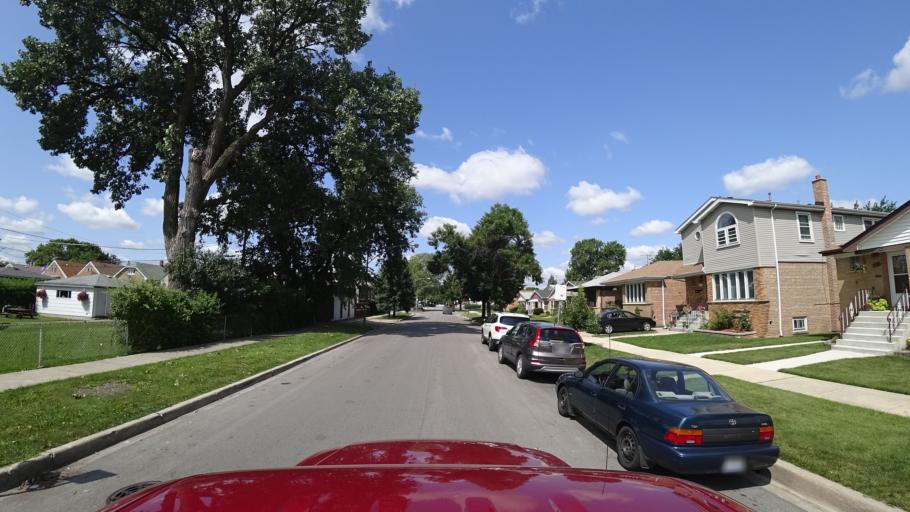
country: US
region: Illinois
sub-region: Cook County
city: Stickney
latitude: 41.8004
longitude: -87.7407
